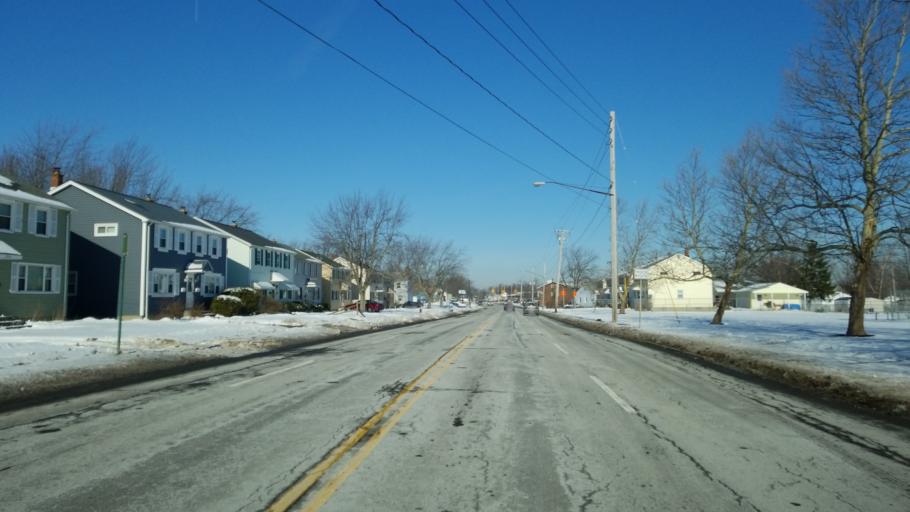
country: US
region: New York
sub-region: Erie County
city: Amherst
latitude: 42.9880
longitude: -78.8354
